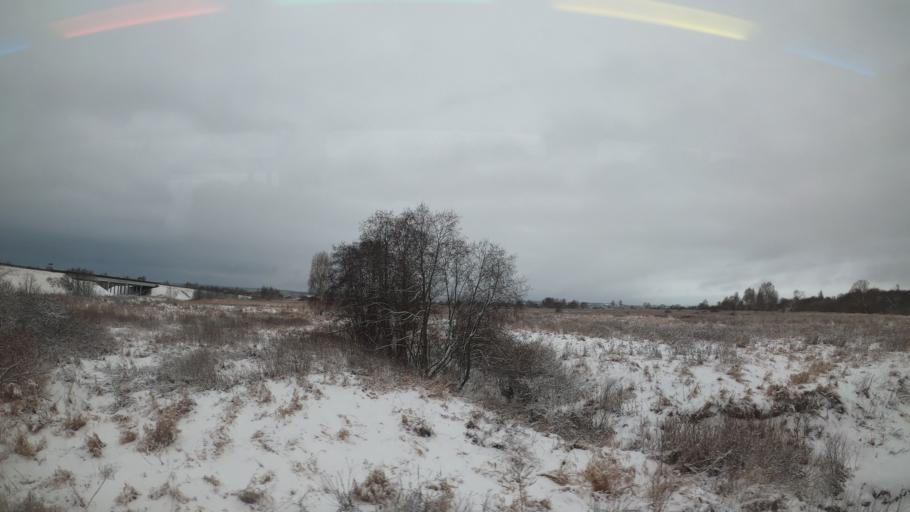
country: RU
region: Jaroslavl
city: Pereslavl'-Zalesskiy
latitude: 56.7168
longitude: 38.9091
